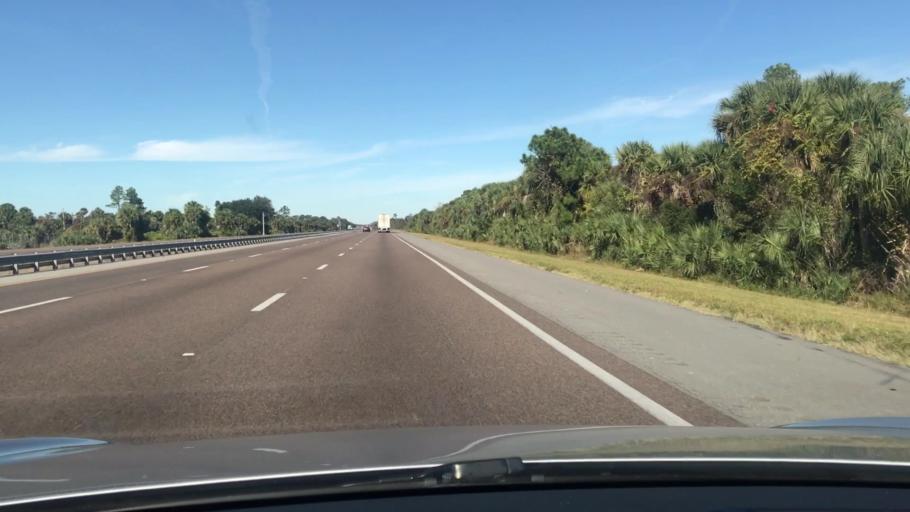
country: US
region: Florida
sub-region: Volusia County
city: Oak Hill
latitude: 28.8019
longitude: -80.9024
